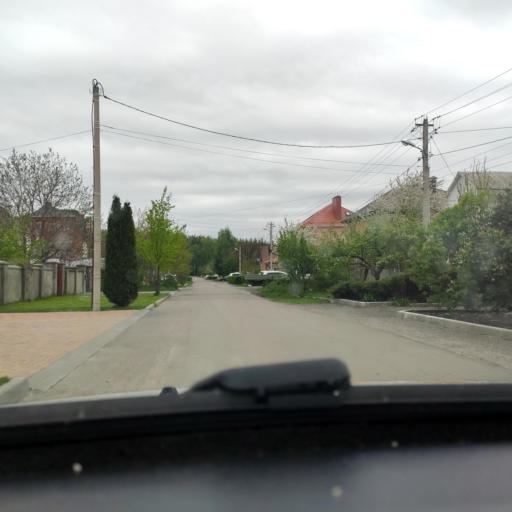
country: RU
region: Voronezj
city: Somovo
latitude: 51.6865
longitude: 39.3098
